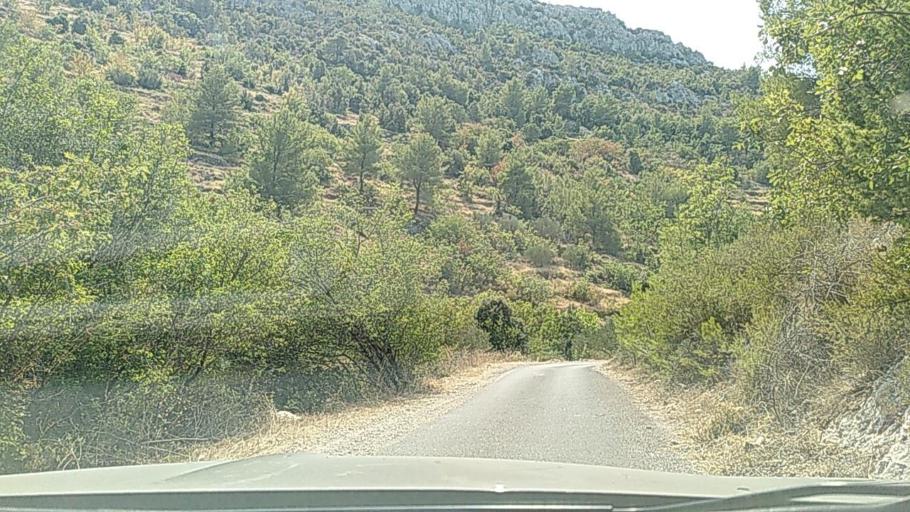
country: HR
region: Splitsko-Dalmatinska
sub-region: Grad Hvar
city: Hvar
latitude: 43.1667
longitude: 16.5100
